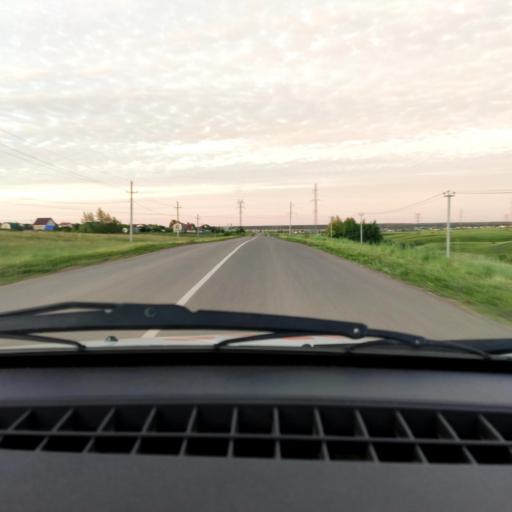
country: RU
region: Bashkortostan
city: Avdon
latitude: 54.5737
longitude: 55.7547
